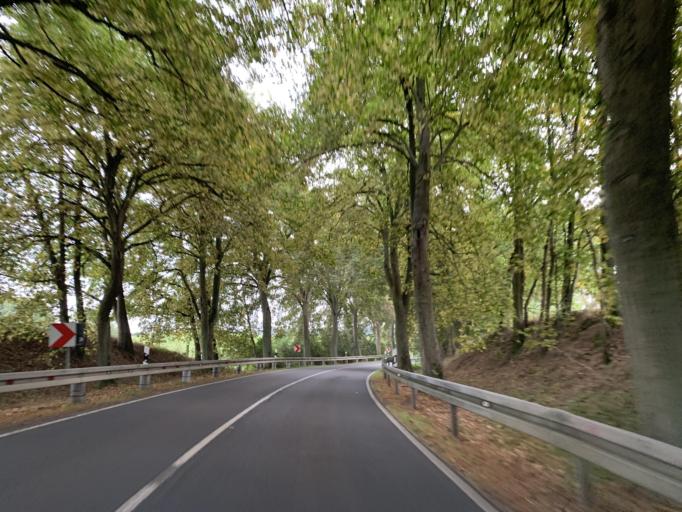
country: DE
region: Mecklenburg-Vorpommern
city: Loitz
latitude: 53.3397
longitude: 13.4834
